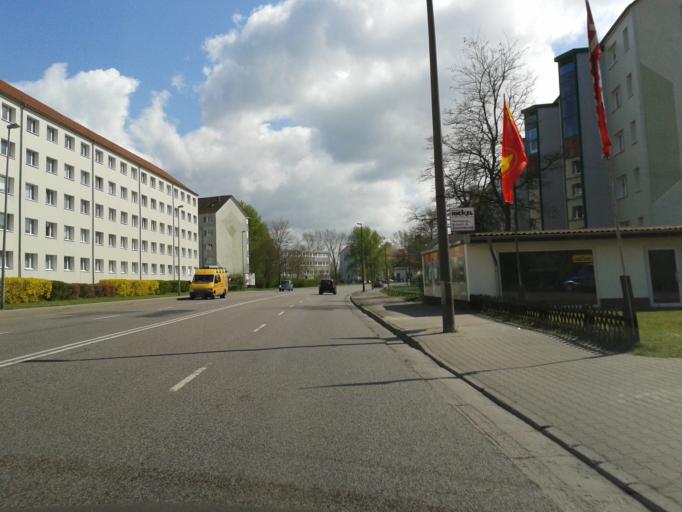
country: DE
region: Saxony-Anhalt
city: Salzwedel
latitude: 52.8564
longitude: 11.1597
